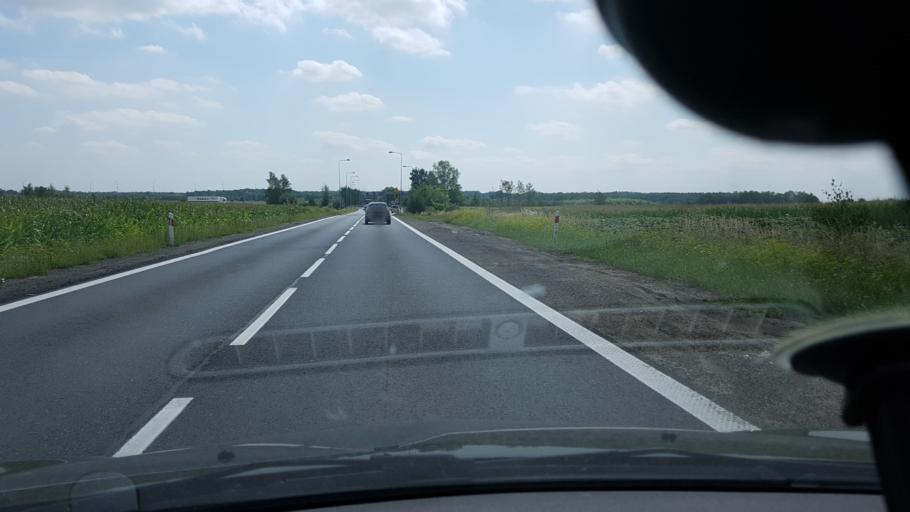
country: PL
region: Silesian Voivodeship
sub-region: Powiat bierunsko-ledzinski
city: Bierun
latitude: 50.0954
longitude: 19.1019
